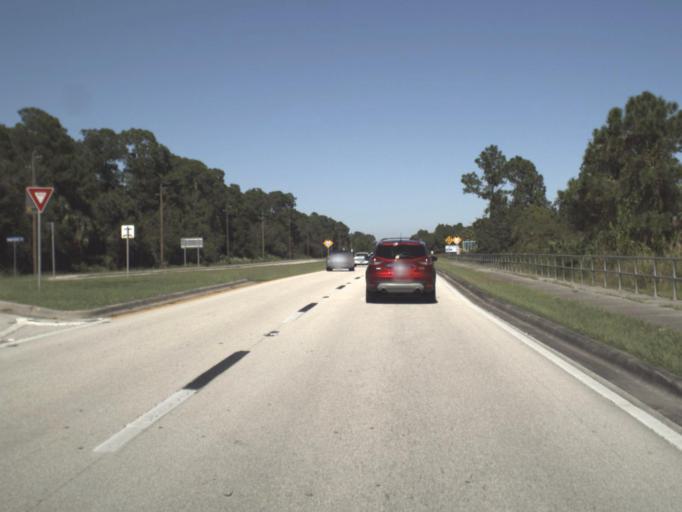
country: US
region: Florida
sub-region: Hendry County
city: LaBelle
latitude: 26.7482
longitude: -81.4600
